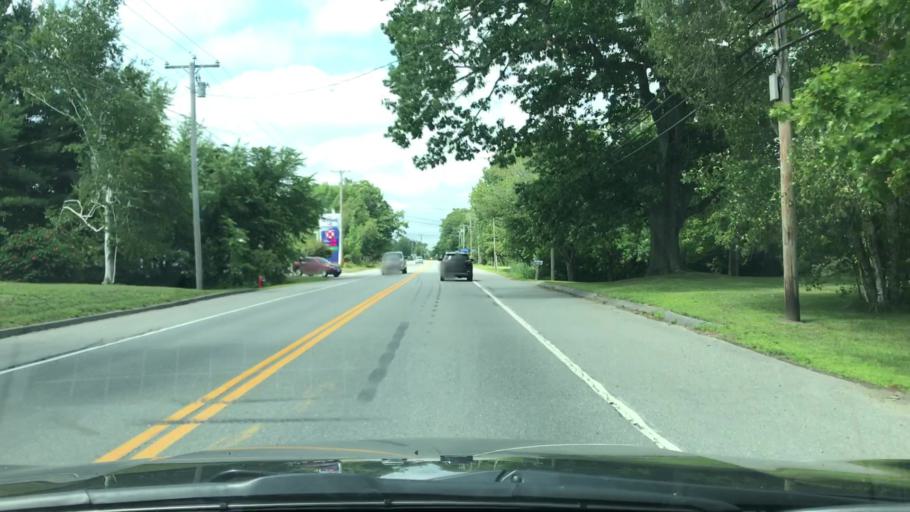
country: US
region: Maine
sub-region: Waldo County
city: Belfast
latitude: 44.4044
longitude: -68.9902
